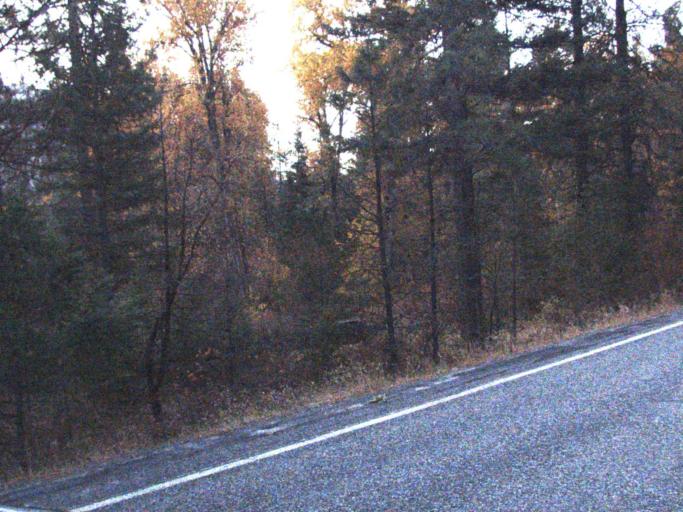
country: US
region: Washington
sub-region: Ferry County
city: Republic
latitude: 48.3405
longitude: -118.7487
